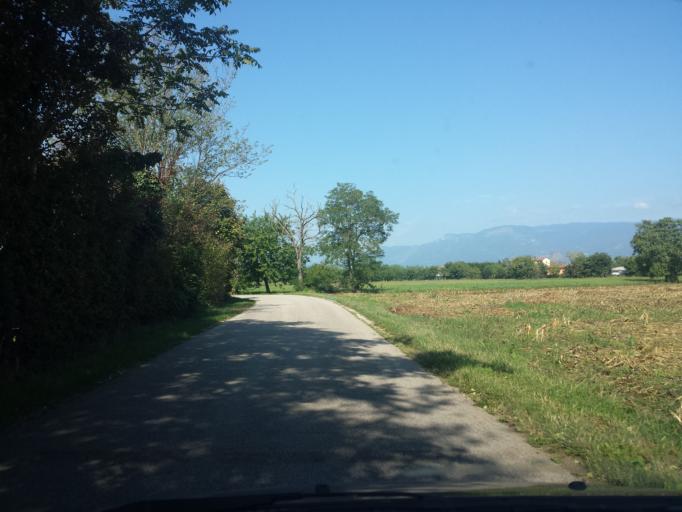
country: IT
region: Veneto
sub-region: Provincia di Vicenza
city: Sandrigo
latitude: 45.6710
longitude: 11.5866
